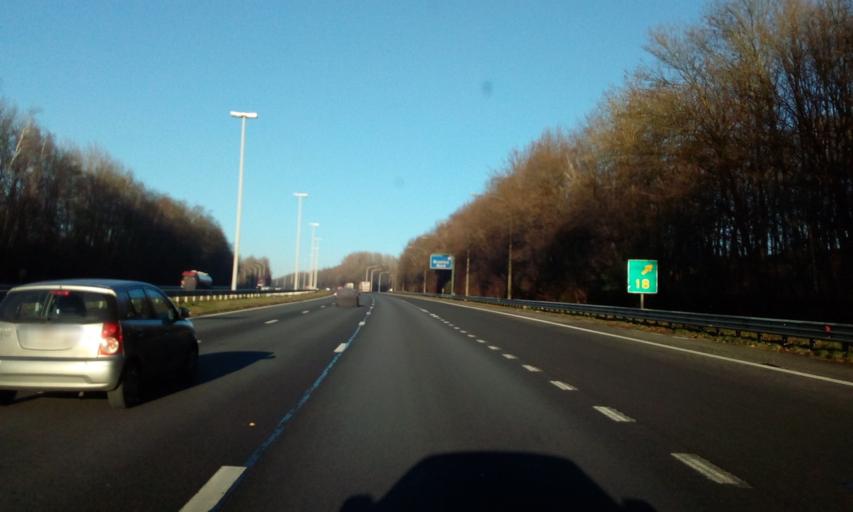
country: BE
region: Wallonia
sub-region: Province du Brabant Wallon
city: Nivelles
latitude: 50.6206
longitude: 4.3046
